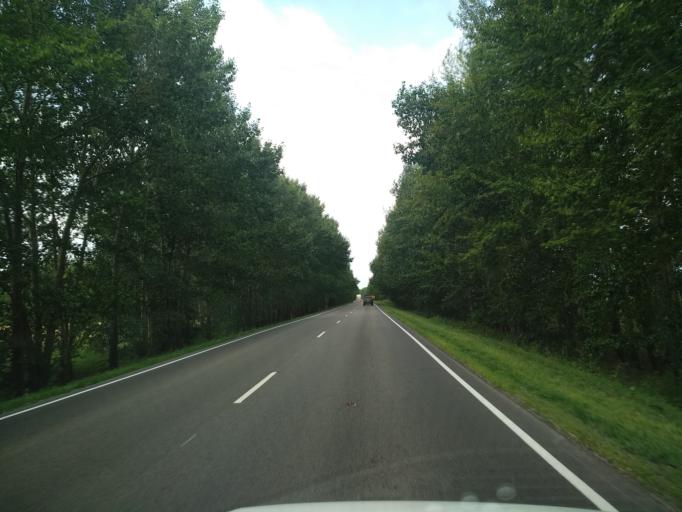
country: RU
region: Voronezj
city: Pereleshino
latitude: 51.8026
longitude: 40.1707
